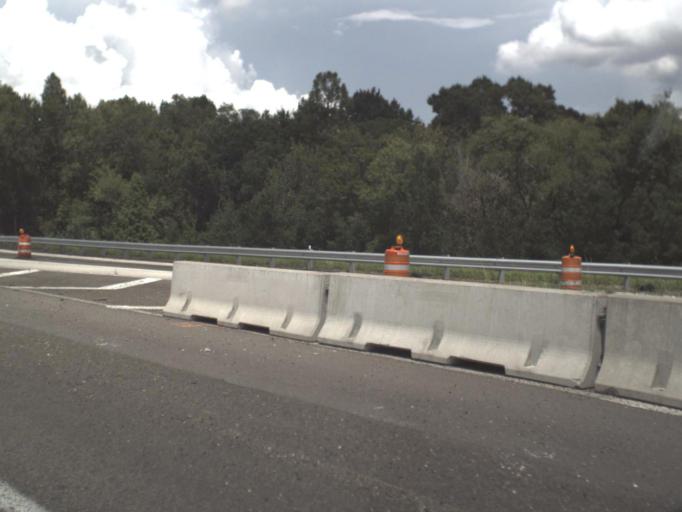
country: US
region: Florida
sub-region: Hillsborough County
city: Temple Terrace
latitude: 28.0571
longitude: -82.3537
